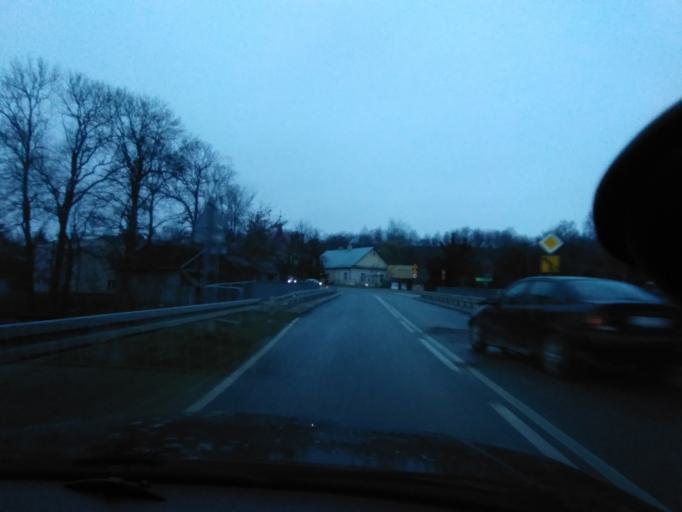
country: PL
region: Subcarpathian Voivodeship
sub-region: Powiat jaroslawski
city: Pruchnik
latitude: 49.9292
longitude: 22.5726
